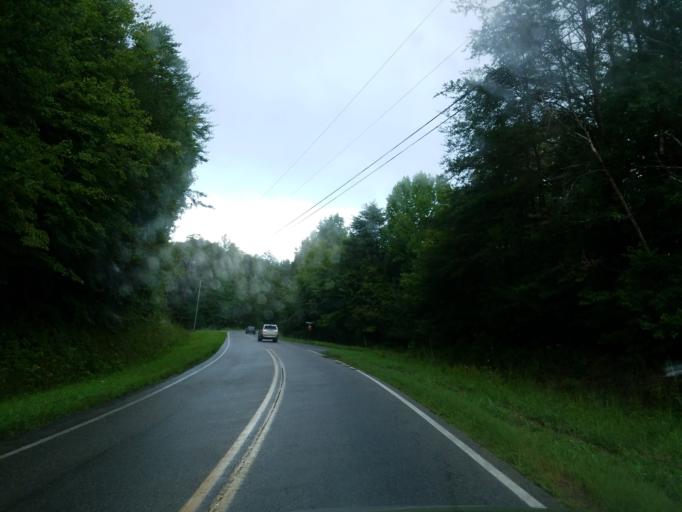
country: US
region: Georgia
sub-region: Lumpkin County
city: Dahlonega
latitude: 34.5522
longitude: -83.8837
